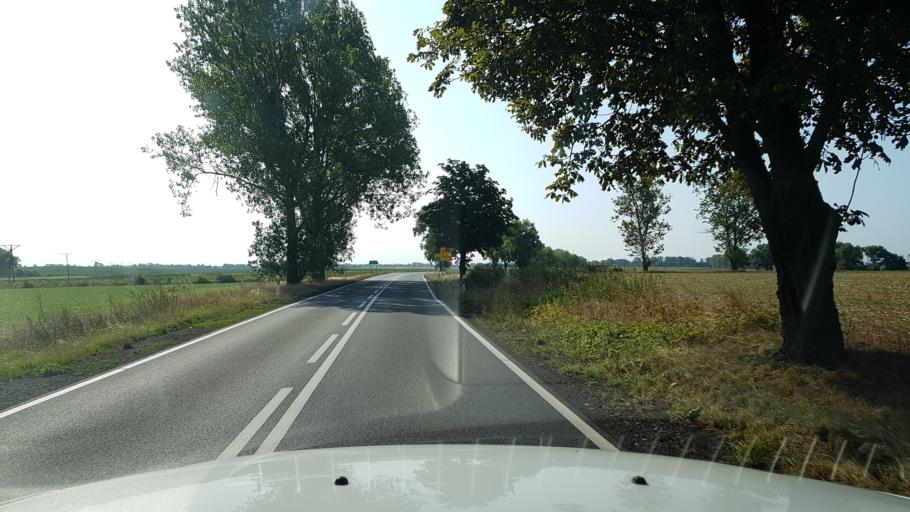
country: PL
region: West Pomeranian Voivodeship
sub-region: Powiat stargardzki
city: Stargard Szczecinski
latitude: 53.2608
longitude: 15.0976
